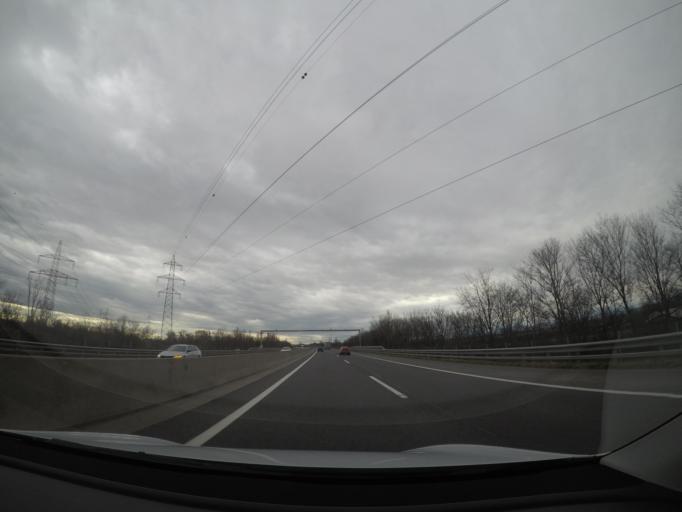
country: AT
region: Lower Austria
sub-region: Politischer Bezirk Baden
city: Trumau
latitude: 47.9788
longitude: 16.3734
